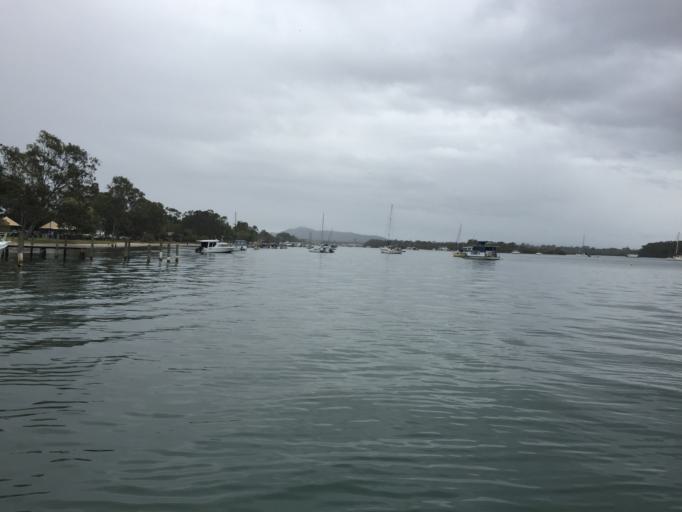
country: AU
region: Queensland
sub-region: Sunshine Coast
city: Noosaville
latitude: -26.3975
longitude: 153.0599
